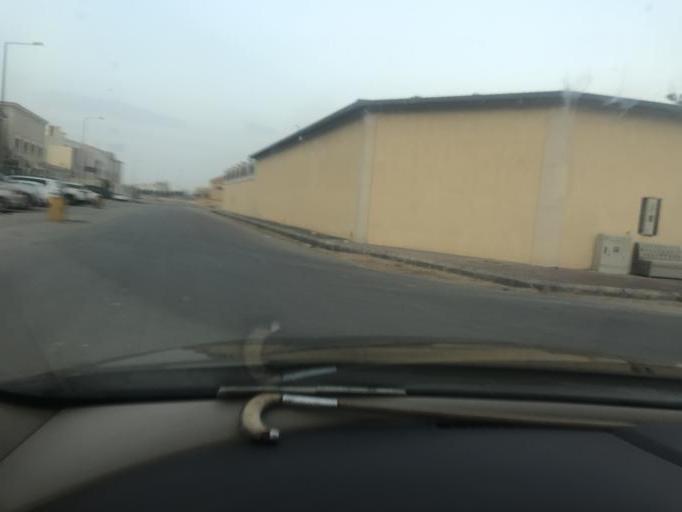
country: SA
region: Ar Riyad
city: Riyadh
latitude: 24.7283
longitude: 46.7482
